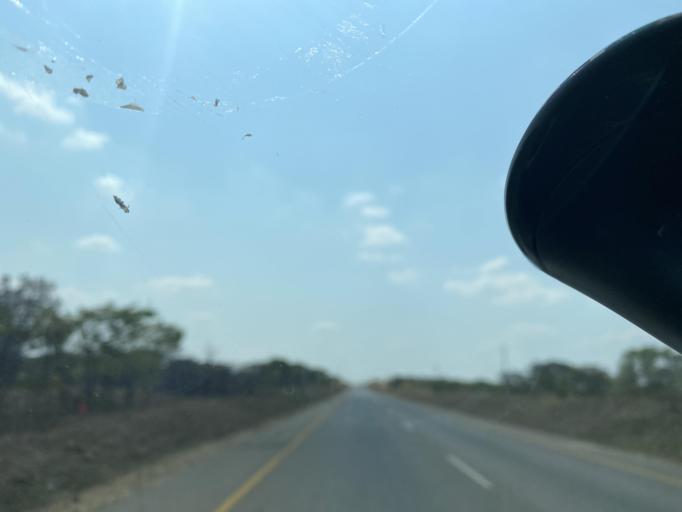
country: ZM
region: Lusaka
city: Chongwe
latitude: -15.5396
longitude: 28.6568
